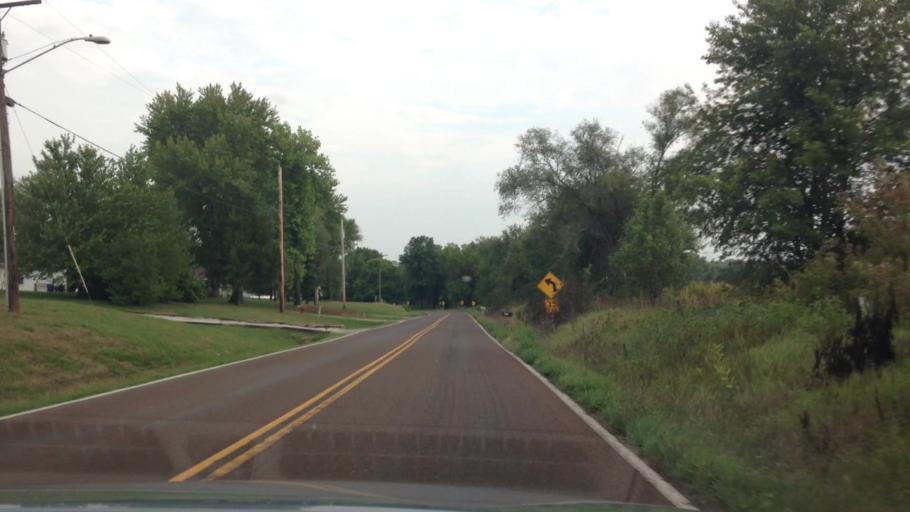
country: US
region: Missouri
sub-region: Clay County
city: Smithville
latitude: 39.3997
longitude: -94.5885
